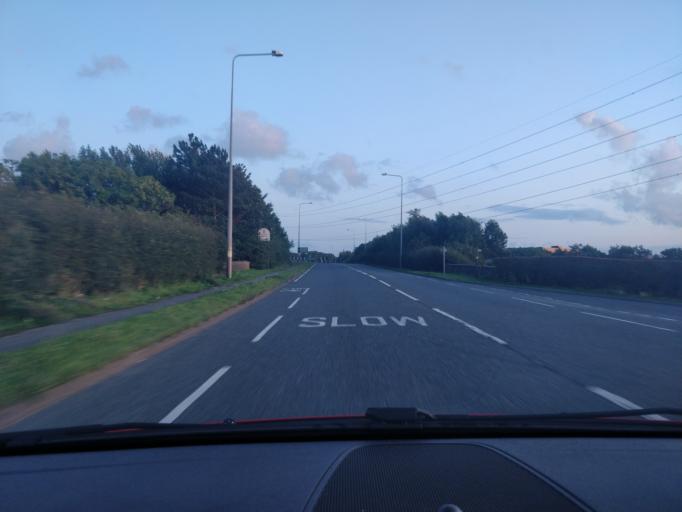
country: GB
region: England
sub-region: Lancashire
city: Tarleton
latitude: 53.6883
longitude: -2.8160
